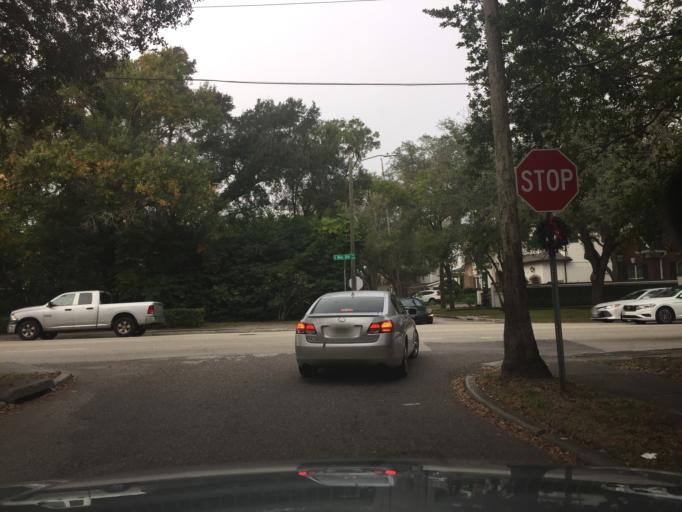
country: US
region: Florida
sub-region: Hillsborough County
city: Tampa
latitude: 27.9324
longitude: -82.4932
